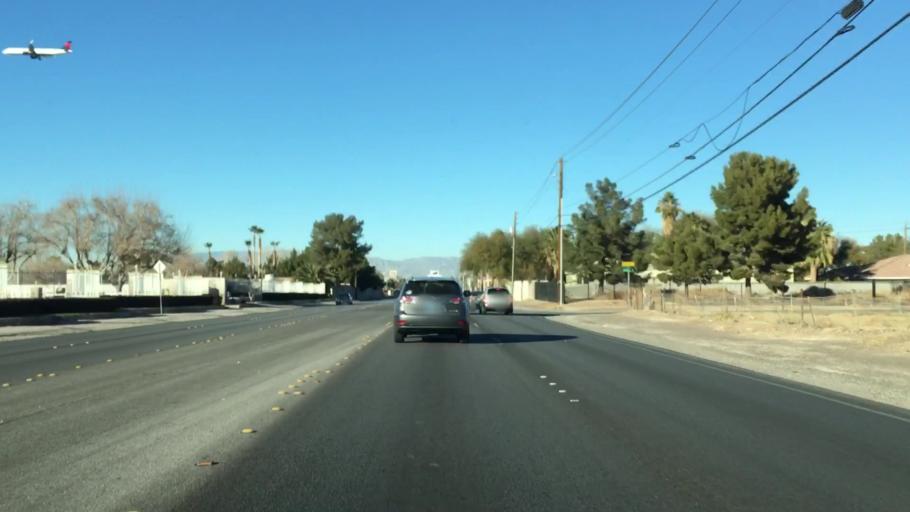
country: US
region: Nevada
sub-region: Clark County
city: Whitney
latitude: 36.0683
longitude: -115.1006
